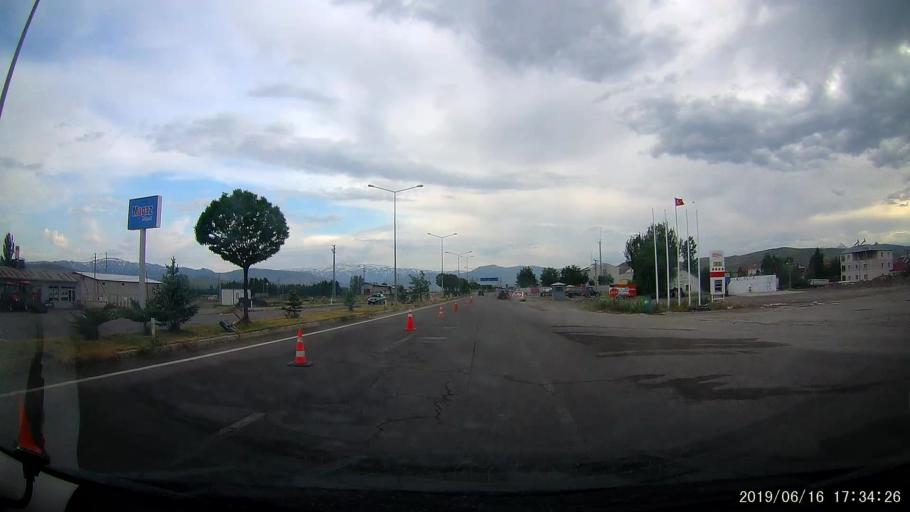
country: TR
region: Erzincan
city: Tercan
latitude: 39.7413
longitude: 40.2686
